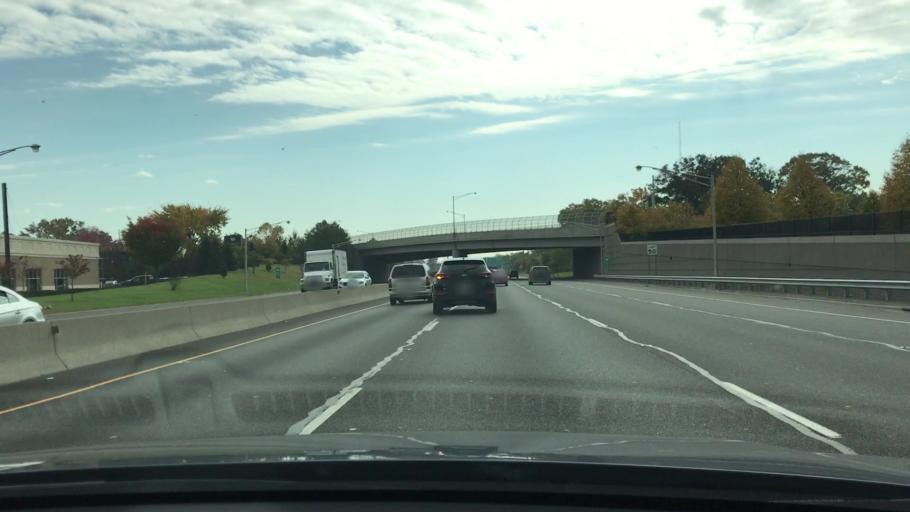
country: US
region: New Jersey
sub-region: Bergen County
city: Maywood
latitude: 40.8918
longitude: -74.0709
